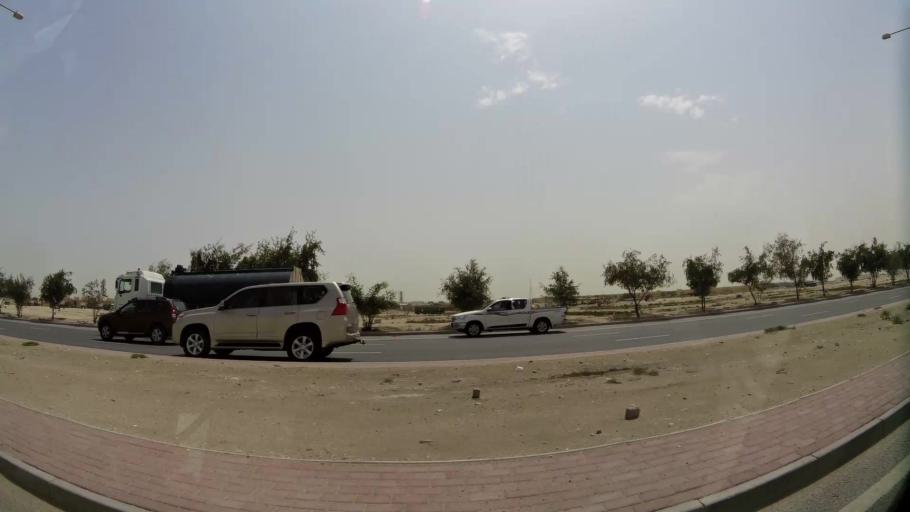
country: QA
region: Baladiyat ar Rayyan
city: Ar Rayyan
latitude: 25.2419
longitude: 51.4129
